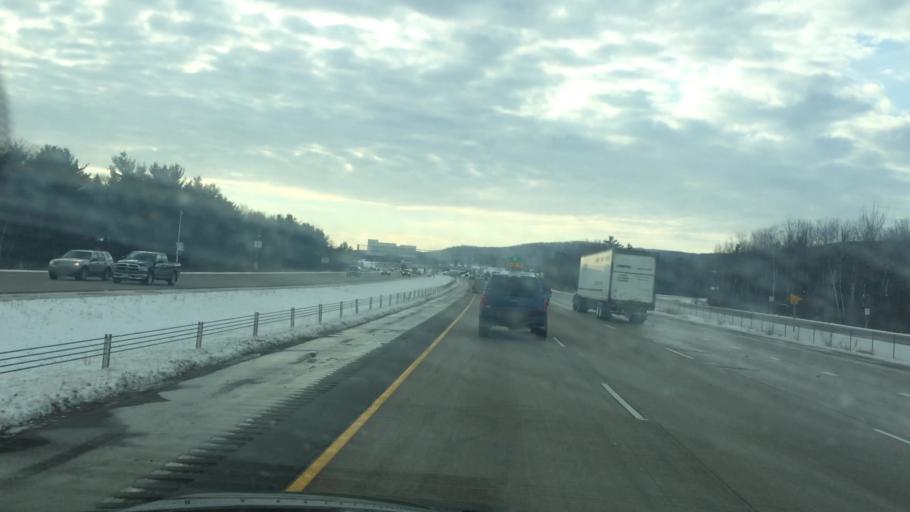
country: US
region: Wisconsin
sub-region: Marathon County
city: Rib Mountain
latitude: 44.9394
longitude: -89.6664
